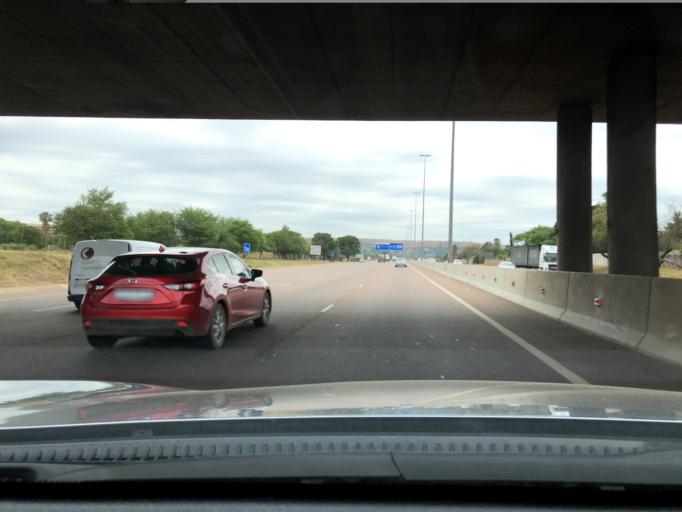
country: ZA
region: Gauteng
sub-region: City of Tshwane Metropolitan Municipality
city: Pretoria
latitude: -25.7212
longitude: 28.2653
